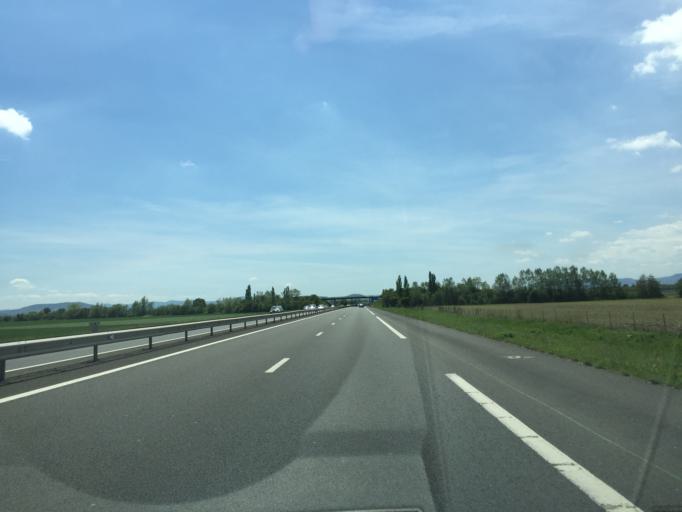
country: FR
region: Auvergne
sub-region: Departement du Puy-de-Dome
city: Menetrol
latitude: 45.8615
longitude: 3.1584
